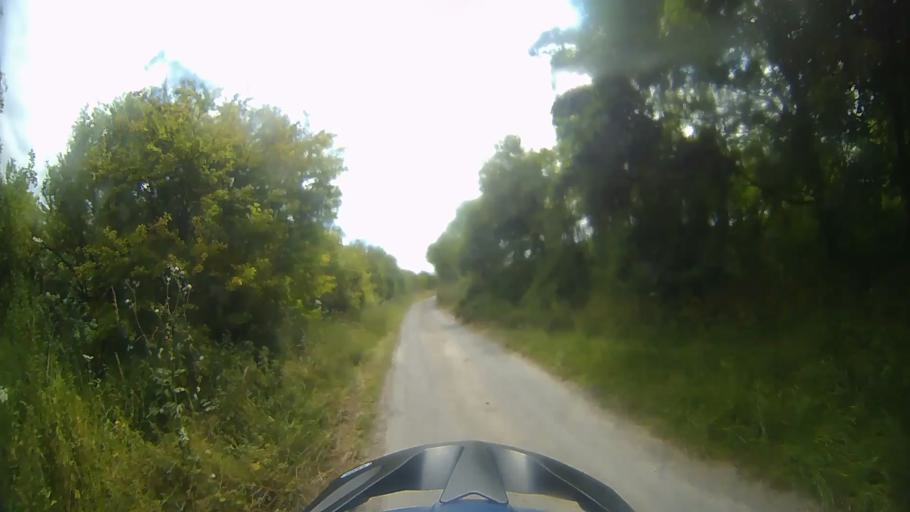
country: GB
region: England
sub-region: Oxfordshire
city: Wantage
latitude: 51.5607
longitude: -1.4456
